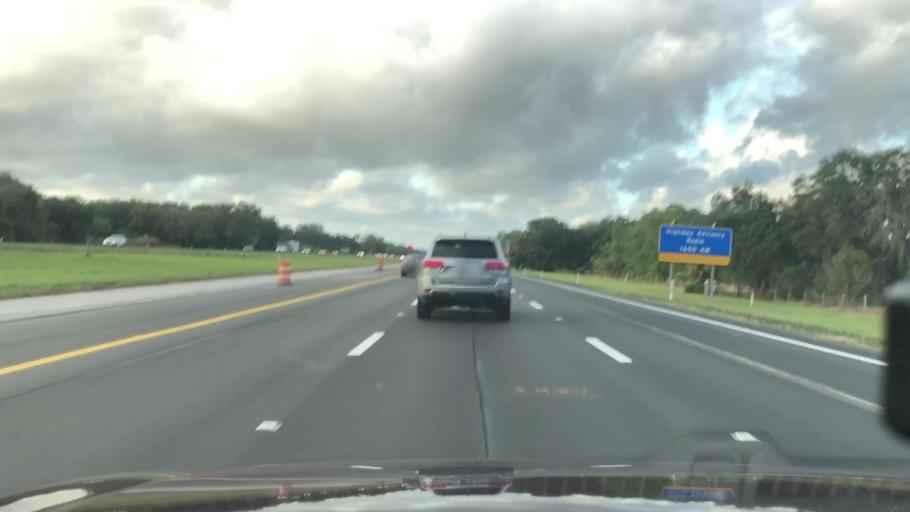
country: US
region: Florida
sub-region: Manatee County
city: Samoset
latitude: 27.4663
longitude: -82.4597
